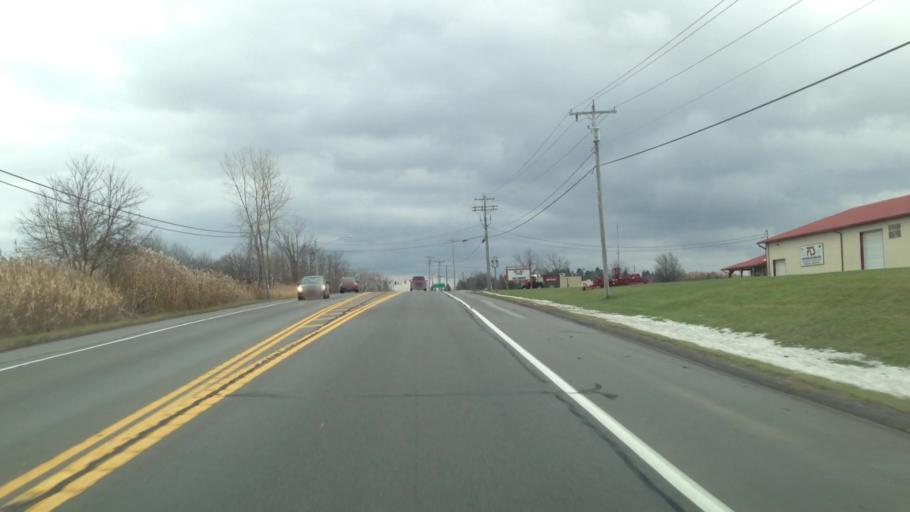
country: US
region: New York
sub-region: Erie County
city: Akron
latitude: 42.9929
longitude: -78.4105
